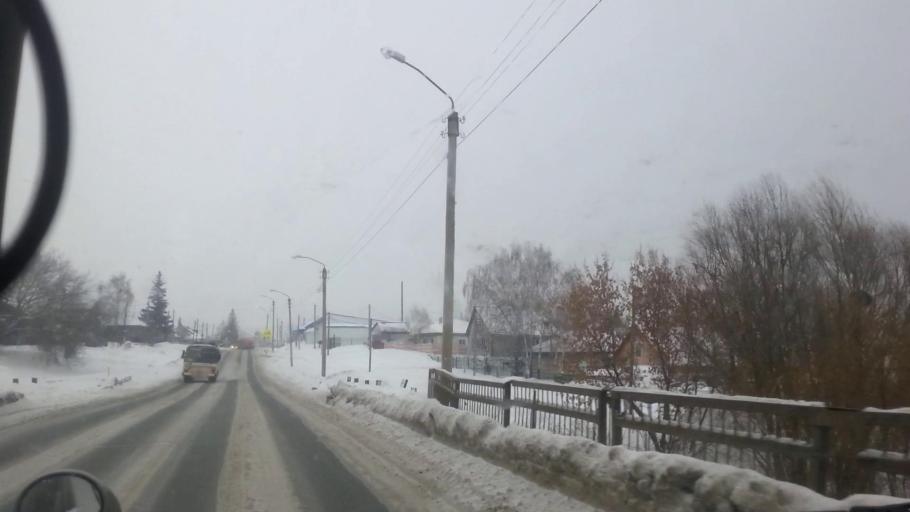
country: RU
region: Altai Krai
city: Vlasikha
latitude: 53.2953
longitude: 83.5800
